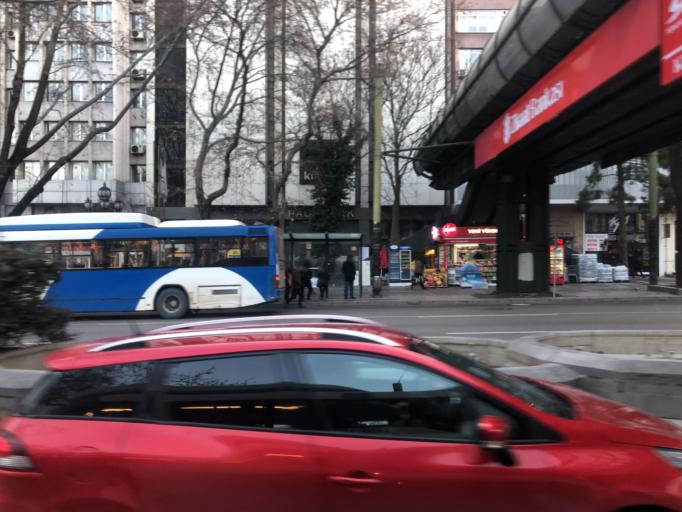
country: TR
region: Ankara
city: Ankara
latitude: 39.9184
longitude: 32.8541
